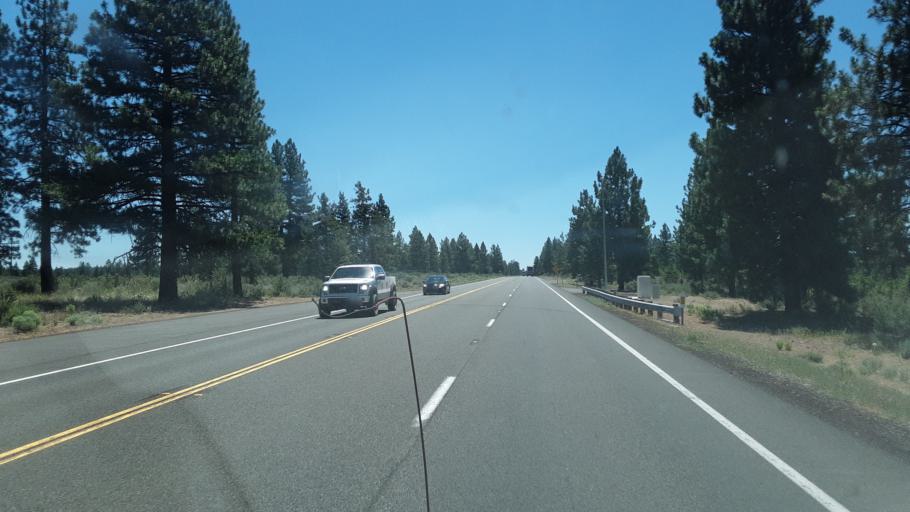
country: US
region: California
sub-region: Siskiyou County
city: Tulelake
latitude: 41.6053
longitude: -121.2080
